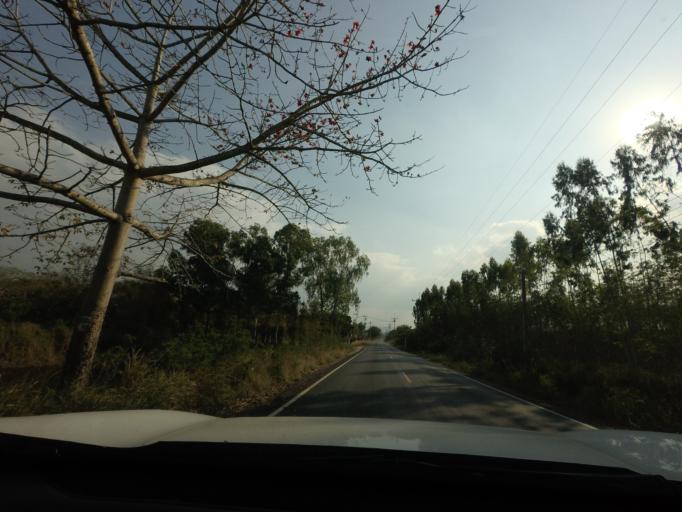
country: TH
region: Nakhon Ratchasima
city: Pak Chong
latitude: 14.6259
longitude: 101.4560
